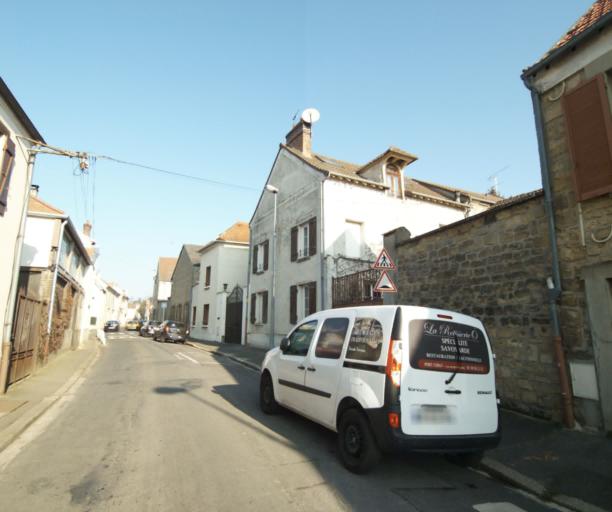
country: FR
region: Ile-de-France
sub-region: Departement du Val-d'Oise
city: Cergy
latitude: 49.0410
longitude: 2.0594
